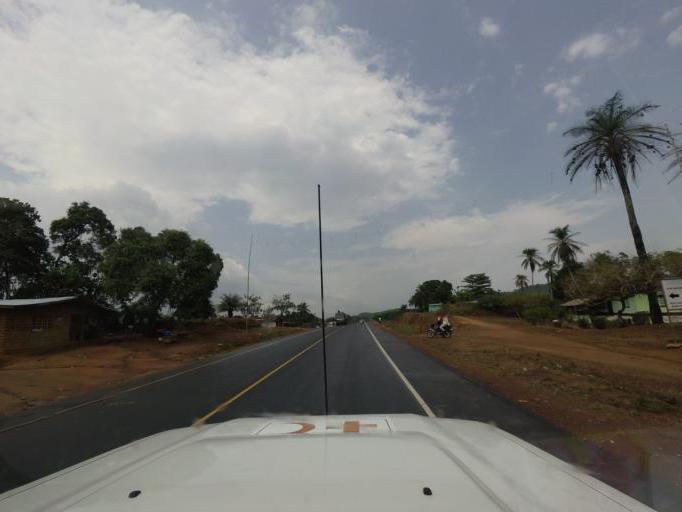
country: LR
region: Montserrado
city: Bensonville City
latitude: 6.4022
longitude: -10.4845
